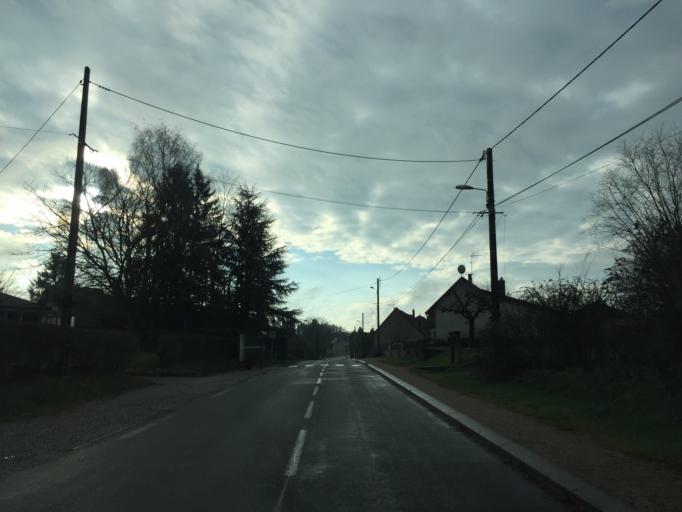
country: FR
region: Franche-Comte
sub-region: Departement du Jura
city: Mont-sous-Vaudrey
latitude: 46.9727
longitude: 5.6046
